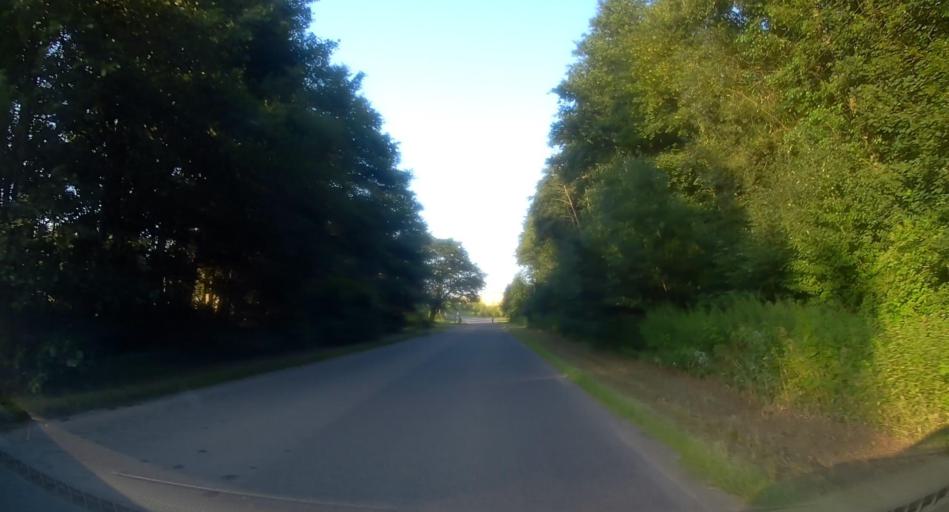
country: PL
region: Lodz Voivodeship
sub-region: Powiat skierniewicki
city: Kowiesy
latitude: 51.8886
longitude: 20.4158
